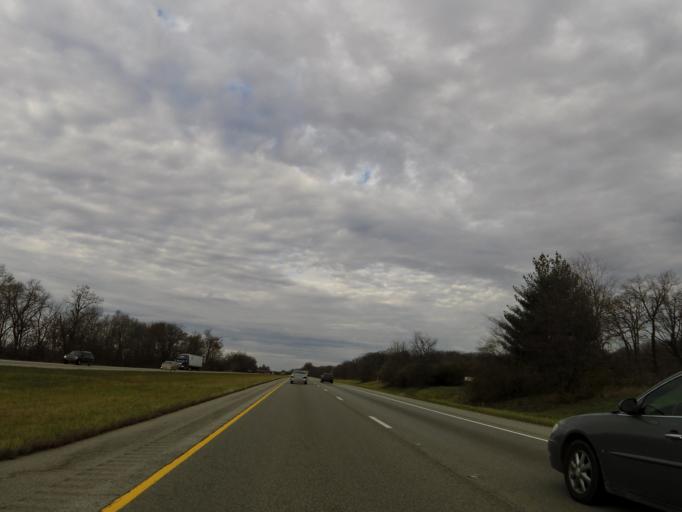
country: US
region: Illinois
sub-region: Clinton County
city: Wamac
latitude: 38.3822
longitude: -89.1173
